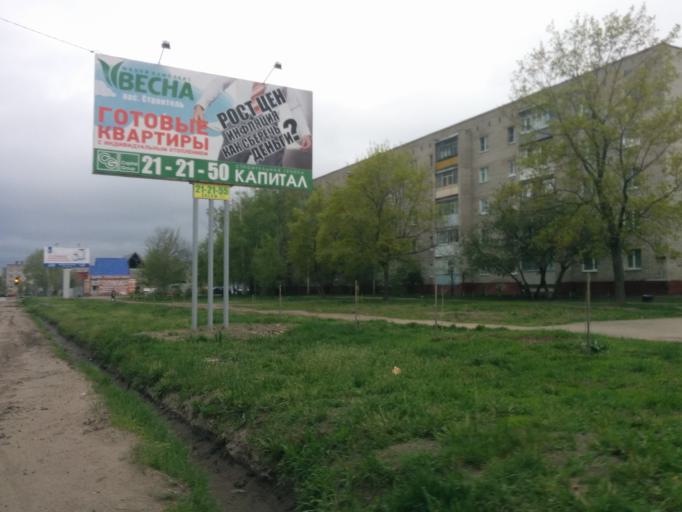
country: RU
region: Tambov
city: Tambov
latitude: 52.7351
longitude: 41.4367
